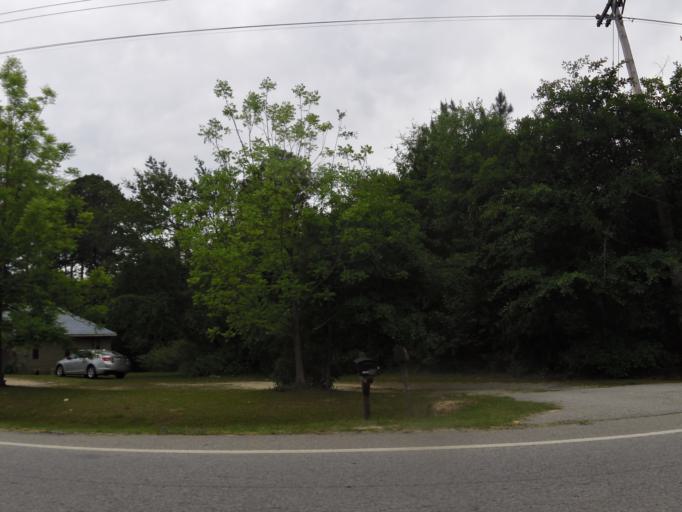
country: US
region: Georgia
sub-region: Candler County
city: Metter
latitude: 32.4341
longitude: -82.2151
